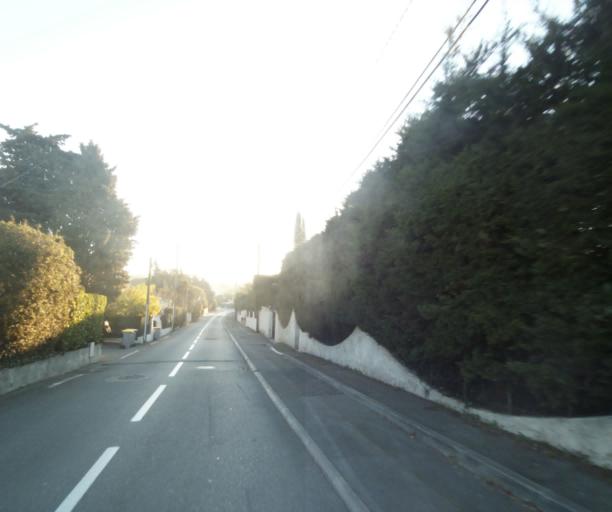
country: FR
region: Provence-Alpes-Cote d'Azur
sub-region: Departement des Alpes-Maritimes
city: Vallauris
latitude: 43.5790
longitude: 7.0865
